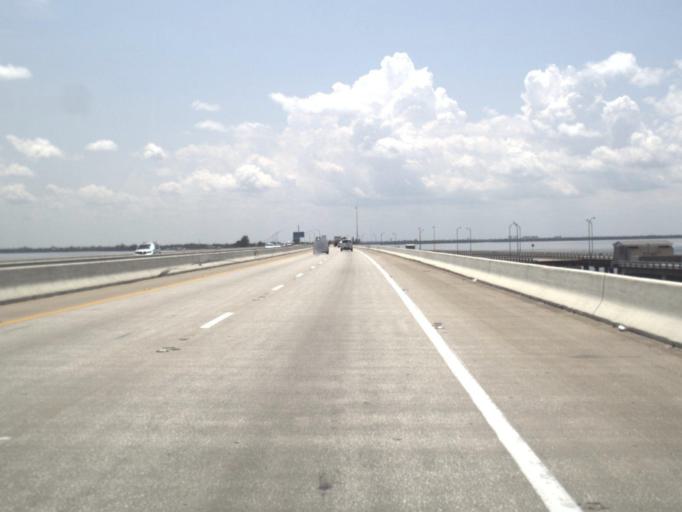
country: US
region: Florida
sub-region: Manatee County
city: Memphis
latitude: 27.5965
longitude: -82.6356
